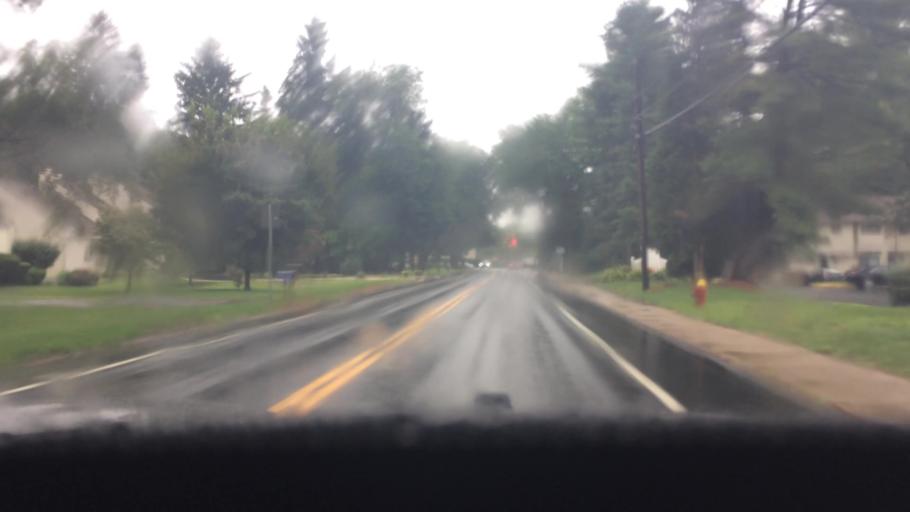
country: US
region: Connecticut
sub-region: Hartford County
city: Blue Hills
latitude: 41.8345
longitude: -72.7335
